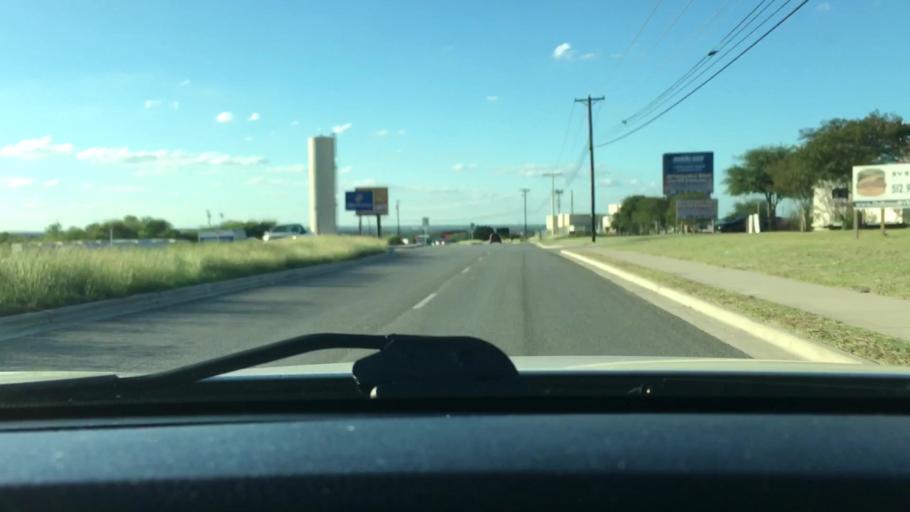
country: US
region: Texas
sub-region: Travis County
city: Windemere
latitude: 30.4796
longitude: -97.6442
